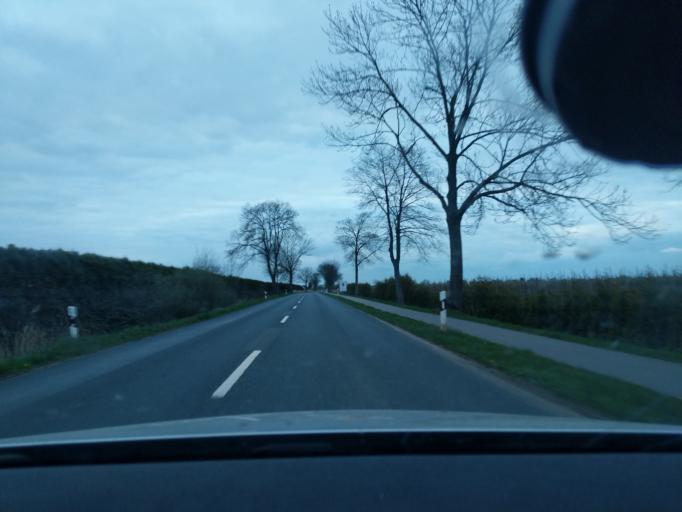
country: DE
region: Lower Saxony
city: Neu Wulmstorf
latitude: 53.5232
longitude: 9.7570
